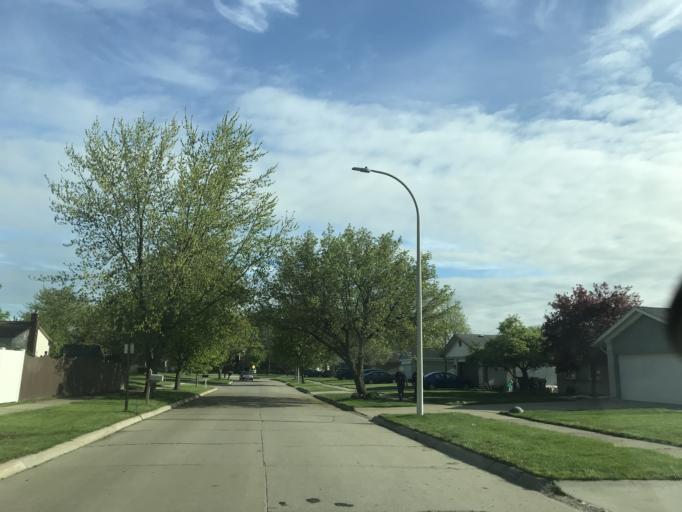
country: US
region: Michigan
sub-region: Wayne County
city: Woodhaven
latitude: 42.1465
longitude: -83.2459
